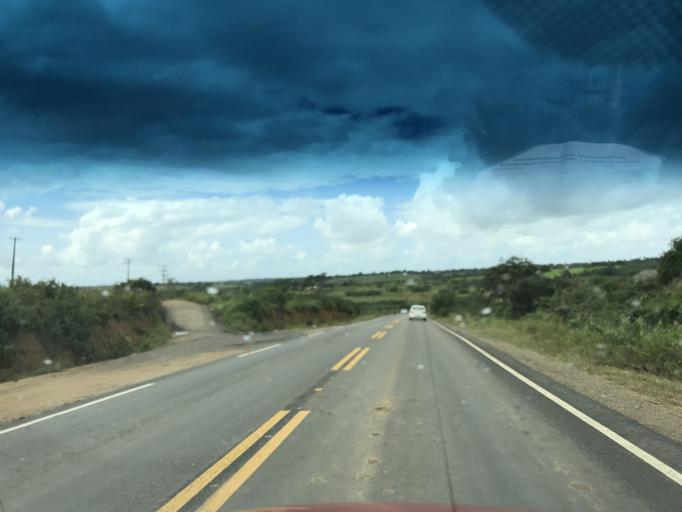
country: BR
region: Bahia
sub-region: Conceicao Do Almeida
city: Conceicao do Almeida
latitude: -12.6791
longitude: -39.2584
